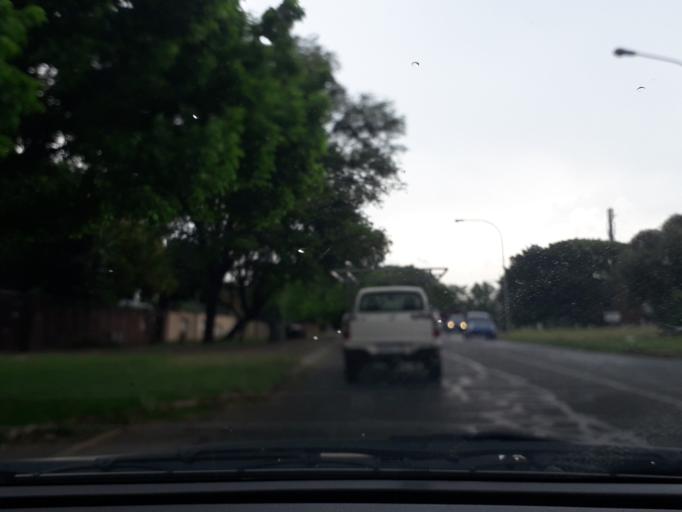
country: ZA
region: Gauteng
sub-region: City of Johannesburg Metropolitan Municipality
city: Johannesburg
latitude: -26.1465
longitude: 28.1036
